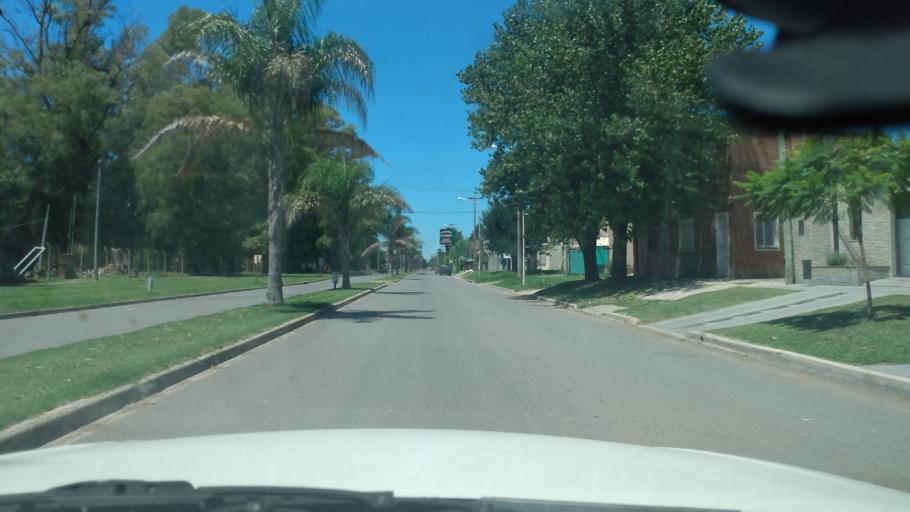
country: AR
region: Buenos Aires
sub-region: Partido de San Andres de Giles
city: San Andres de Giles
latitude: -34.4420
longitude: -59.4388
